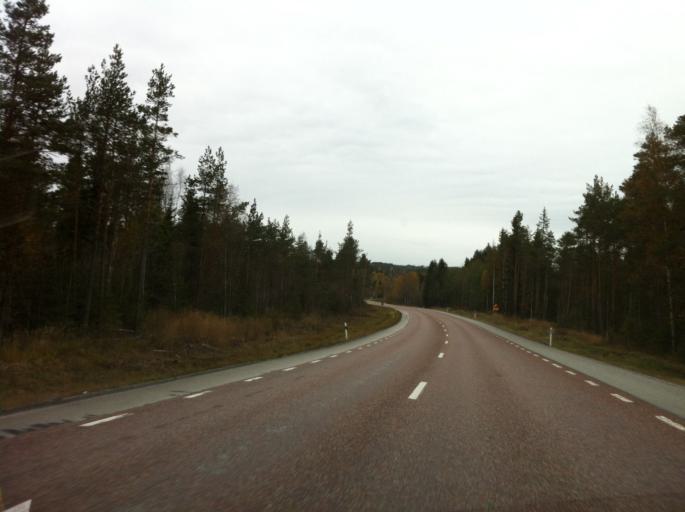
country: SE
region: Dalarna
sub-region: Ludvika Kommun
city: Grangesberg
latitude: 59.9827
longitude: 15.0208
